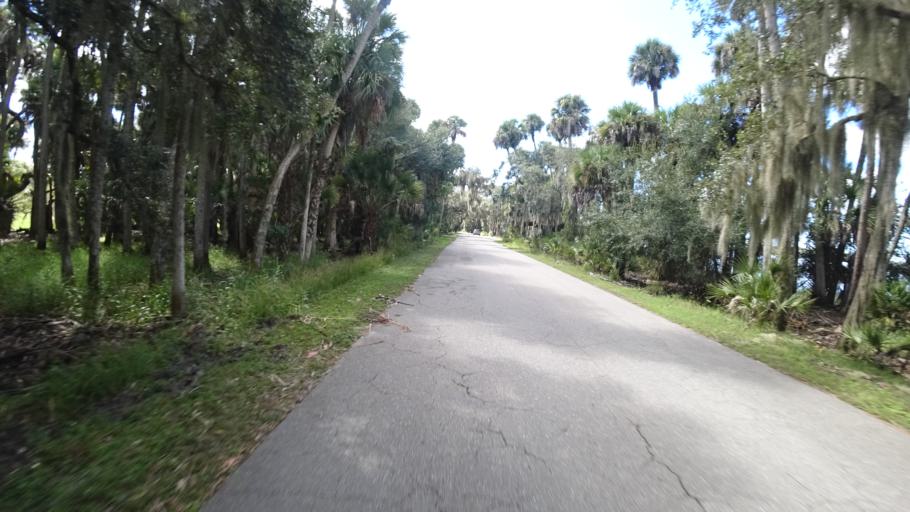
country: US
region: Florida
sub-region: Sarasota County
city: Lake Sarasota
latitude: 27.2669
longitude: -82.2848
